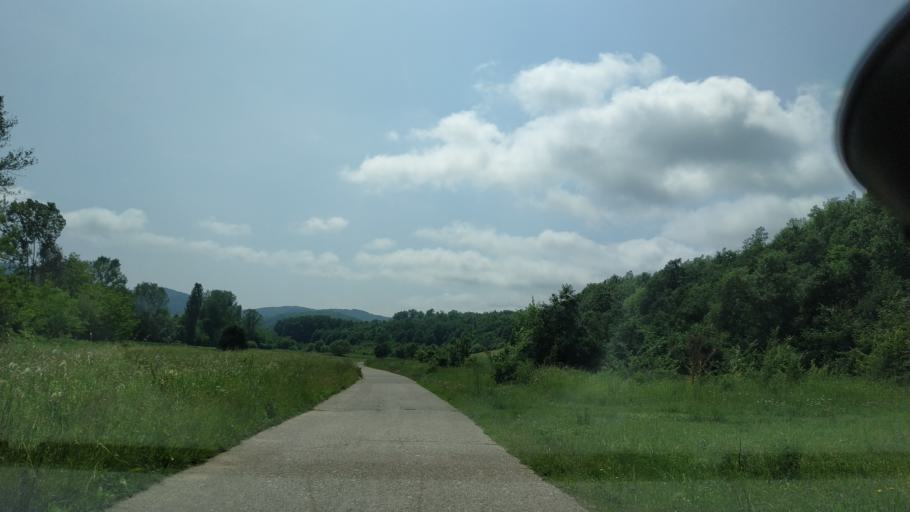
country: RS
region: Central Serbia
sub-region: Nisavski Okrug
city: Aleksinac
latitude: 43.4257
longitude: 21.7229
